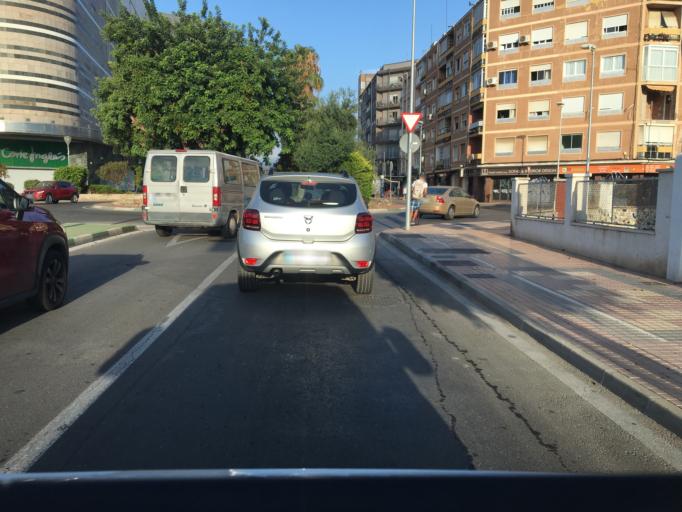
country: ES
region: Murcia
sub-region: Murcia
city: Cartagena
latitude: 37.6148
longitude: -0.9929
